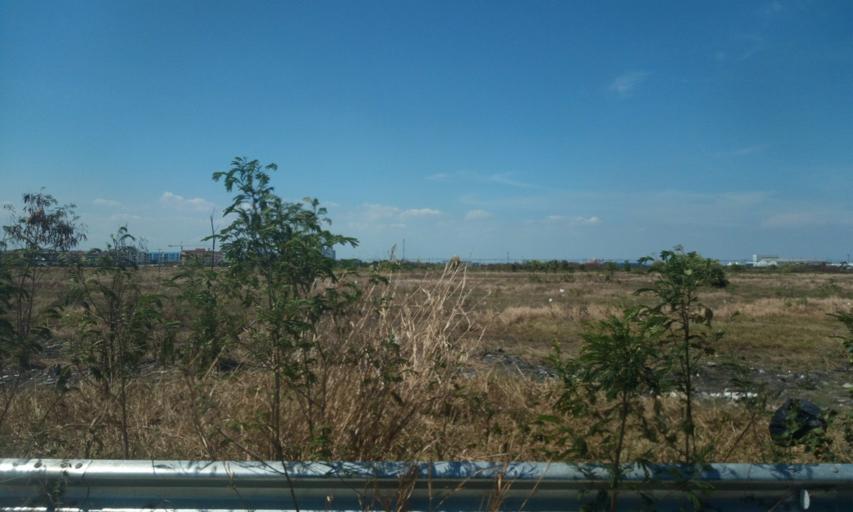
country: TH
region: Samut Prakan
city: Bang Bo District
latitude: 13.5531
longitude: 100.7825
